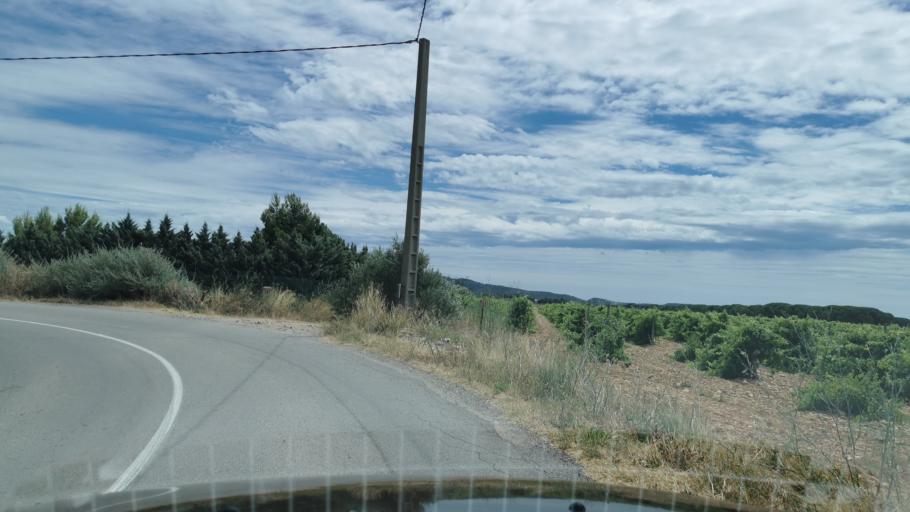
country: FR
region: Languedoc-Roussillon
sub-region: Departement de l'Aude
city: Narbonne
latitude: 43.1464
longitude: 3.0066
